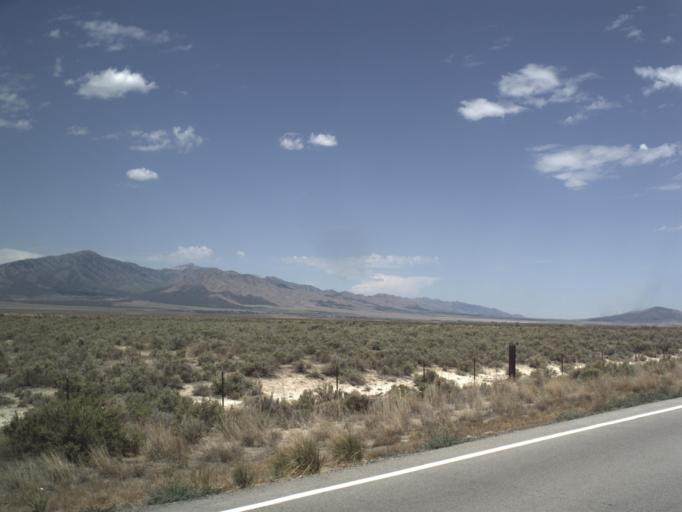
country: US
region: Utah
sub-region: Tooele County
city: Tooele
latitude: 40.2499
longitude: -112.3995
